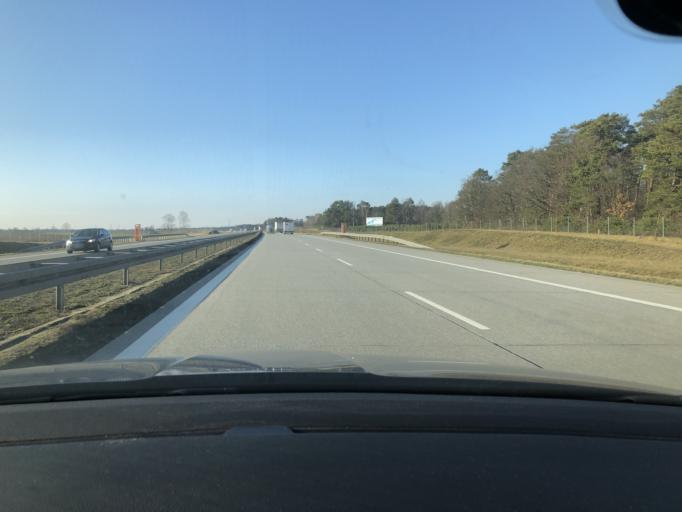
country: PL
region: Lubusz
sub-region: Powiat sulecinski
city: Torzym
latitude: 52.3201
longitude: 15.1901
